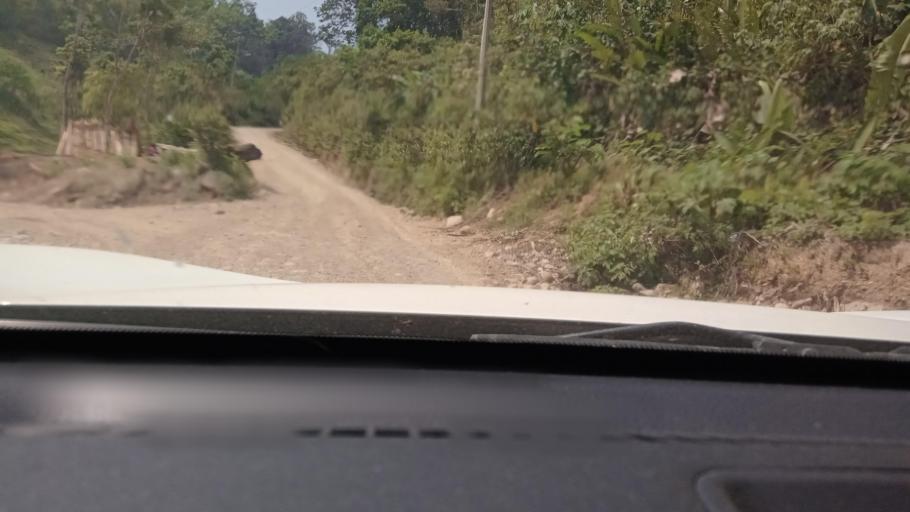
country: MX
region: Tabasco
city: Chontalpa
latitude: 17.4864
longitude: -93.6701
